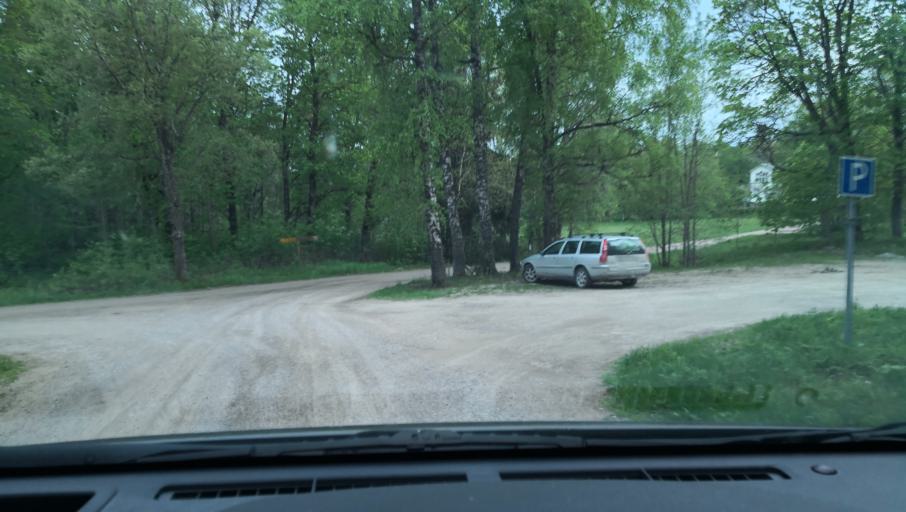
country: SE
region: Vaestmanland
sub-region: Skinnskattebergs Kommun
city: Skinnskatteberg
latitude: 59.7292
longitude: 15.4745
